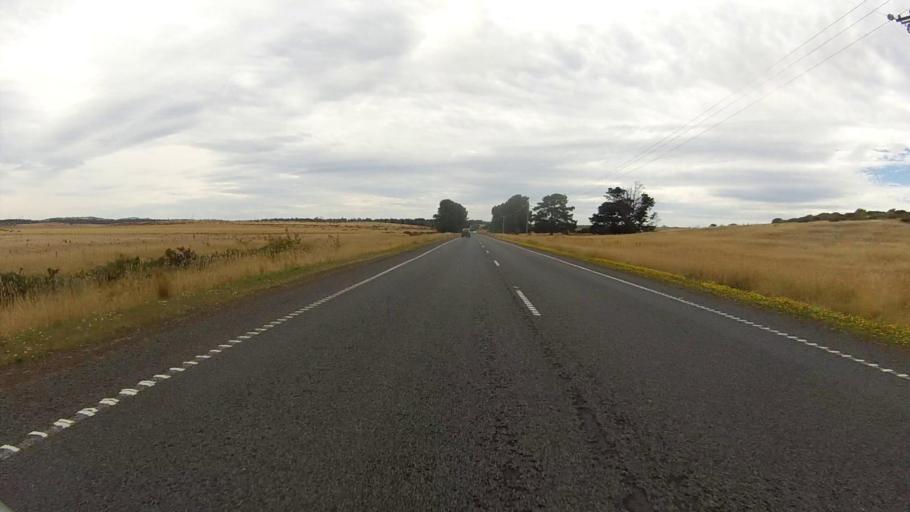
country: AU
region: Tasmania
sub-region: Northern Midlands
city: Evandale
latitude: -41.8518
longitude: 147.4515
